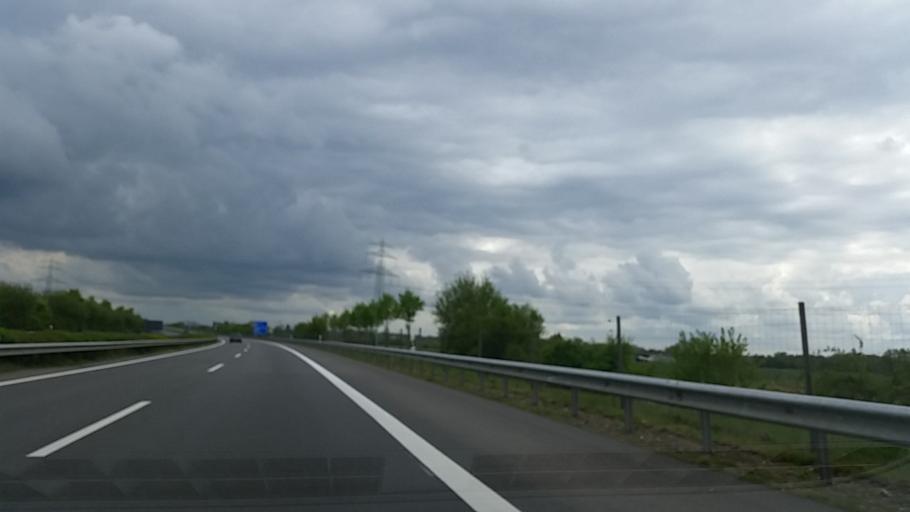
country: DE
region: Lower Saxony
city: Neuenkirchen
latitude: 53.5207
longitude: 9.5848
